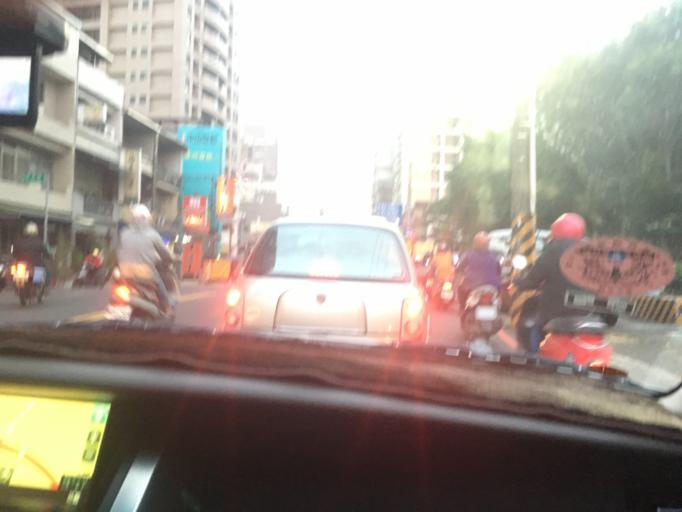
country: TW
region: Taiwan
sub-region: Hsinchu
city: Hsinchu
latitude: 24.7968
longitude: 120.9599
